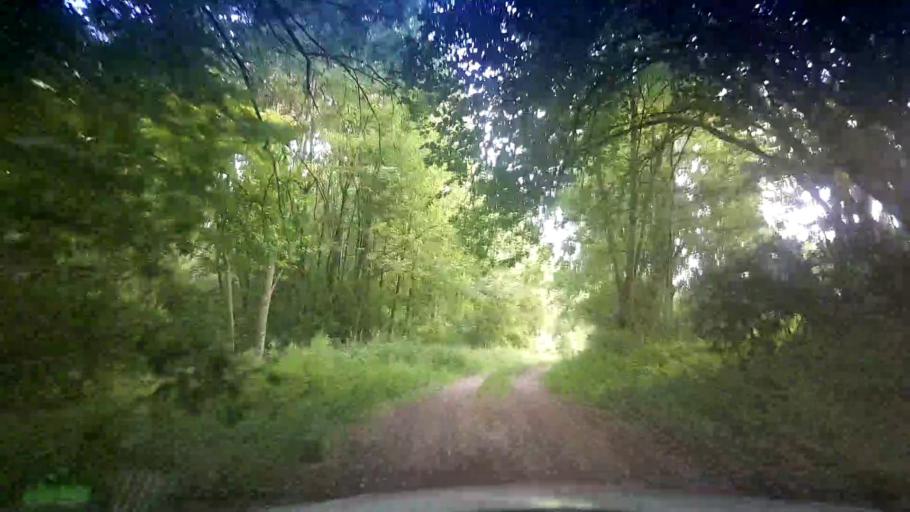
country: DE
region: Bavaria
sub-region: Upper Franconia
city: Memmelsdorf
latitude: 49.9529
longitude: 10.9869
